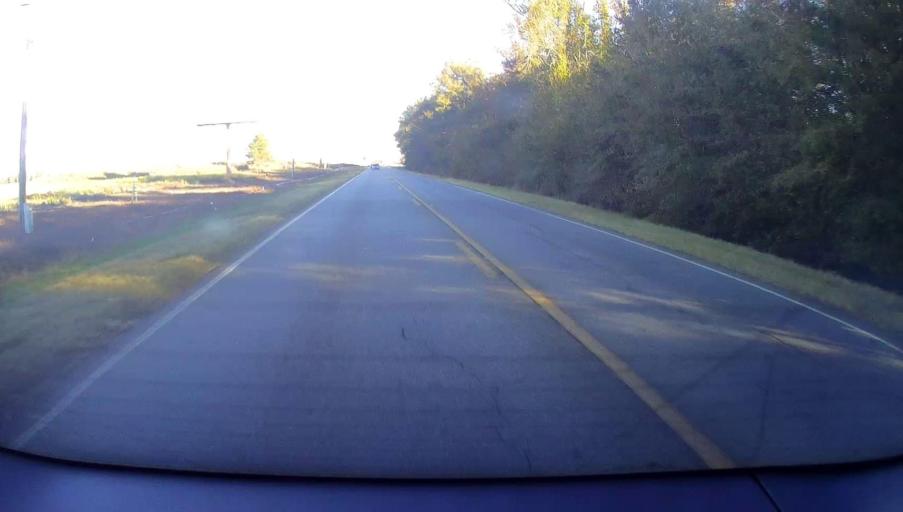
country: US
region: Georgia
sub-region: Houston County
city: Centerville
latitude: 32.5823
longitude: -83.7199
